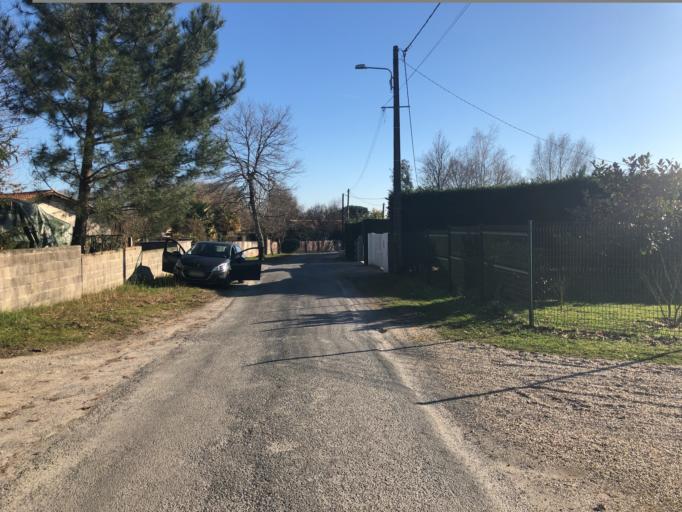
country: FR
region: Aquitaine
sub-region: Departement de la Gironde
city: Castelnau-de-Medoc
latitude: 45.0316
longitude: -0.8036
